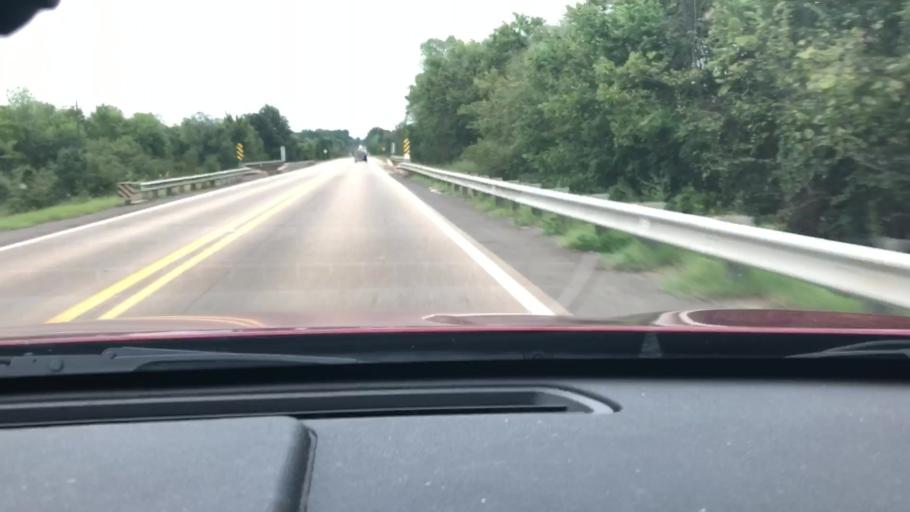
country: US
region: Arkansas
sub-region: Lafayette County
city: Lewisville
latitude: 33.3577
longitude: -93.6378
